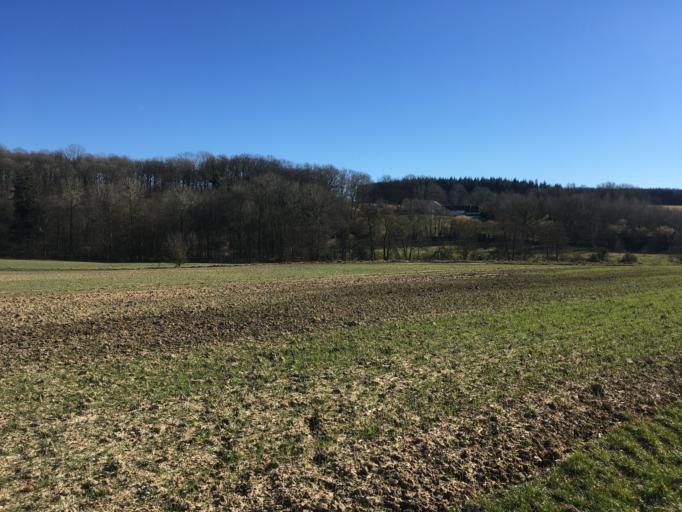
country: BE
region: Wallonia
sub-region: Province de Namur
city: Gesves
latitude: 50.3611
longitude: 5.0869
